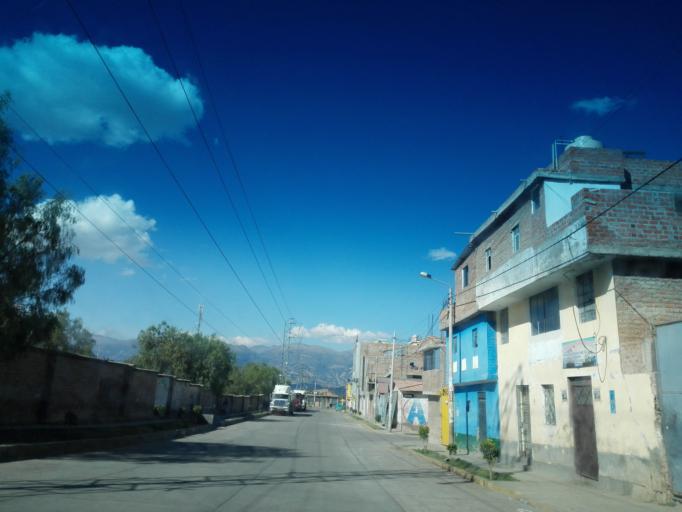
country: PE
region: Ayacucho
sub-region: Provincia de Huamanga
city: Ayacucho
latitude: -13.1493
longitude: -74.2159
